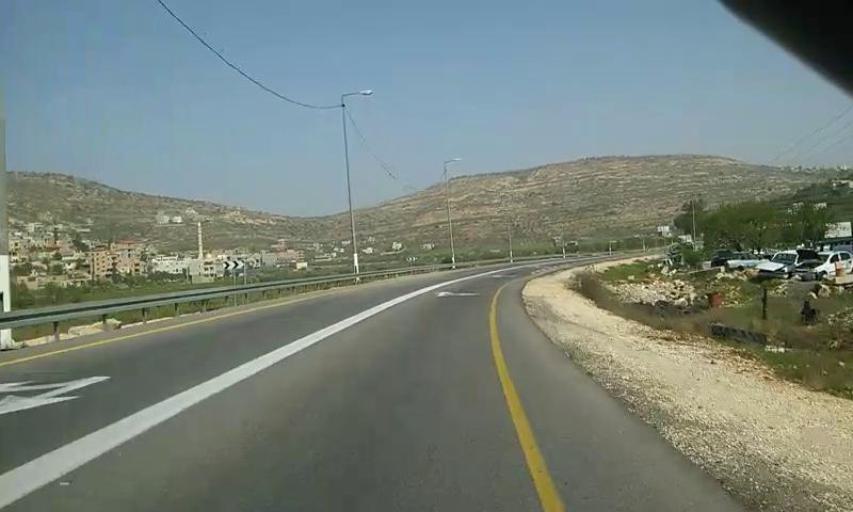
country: PS
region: West Bank
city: Al Lubban ash Sharqiyah
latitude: 32.0713
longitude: 35.2482
